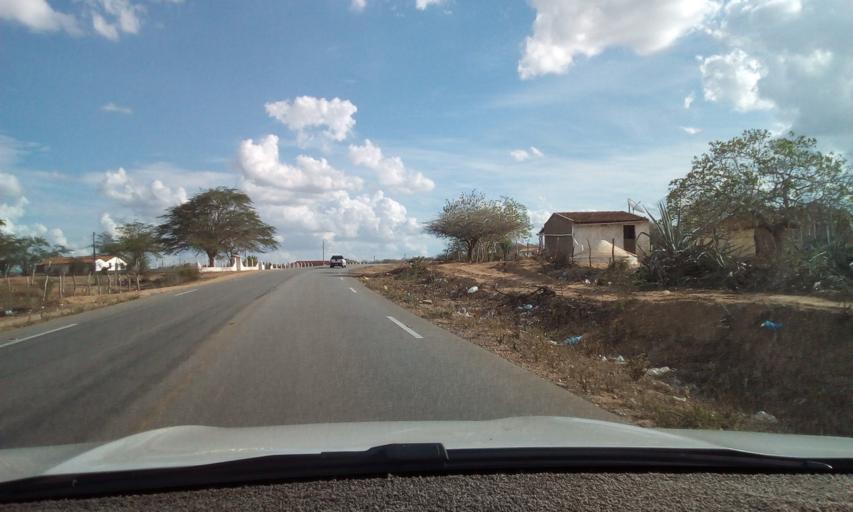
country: BR
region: Paraiba
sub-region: Soledade
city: Soledade
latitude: -6.9222
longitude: -36.3852
